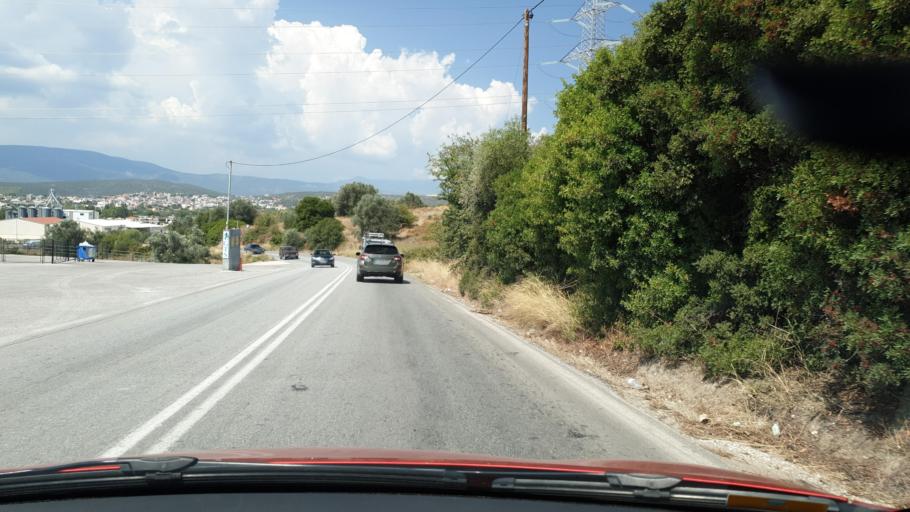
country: GR
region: Central Greece
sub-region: Nomos Evvoias
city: Aliveri
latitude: 38.3966
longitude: 24.0649
